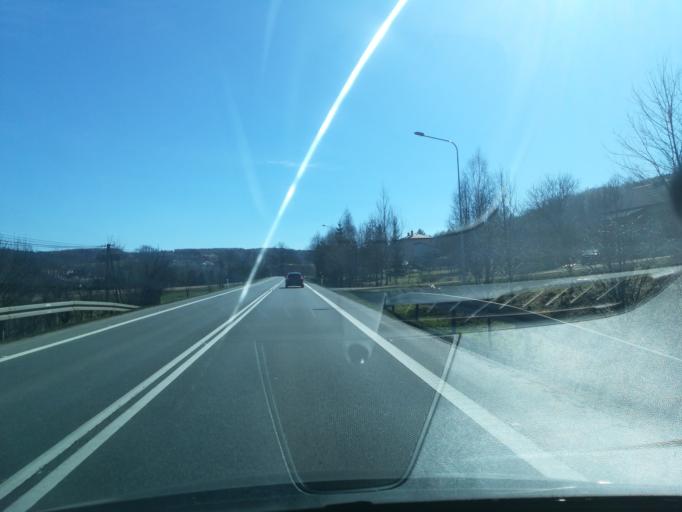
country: PL
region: Subcarpathian Voivodeship
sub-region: Powiat strzyzowski
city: Polomia
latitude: 49.8865
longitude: 21.8985
